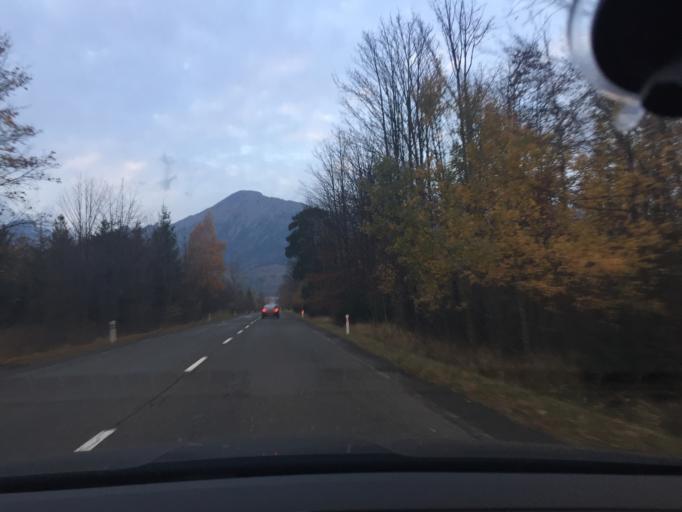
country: SK
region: Presovsky
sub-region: Okres Poprad
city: Vysoke Tatry
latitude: 49.1263
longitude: 20.2431
